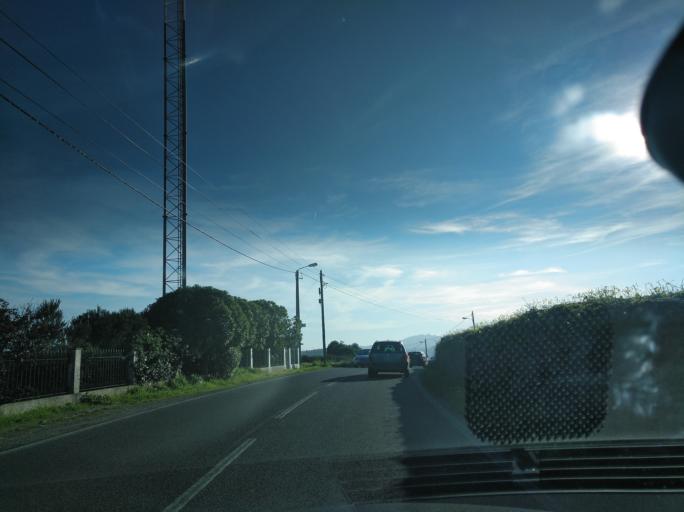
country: PT
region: Lisbon
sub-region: Mafra
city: Mafra
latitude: 38.8984
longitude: -9.3261
